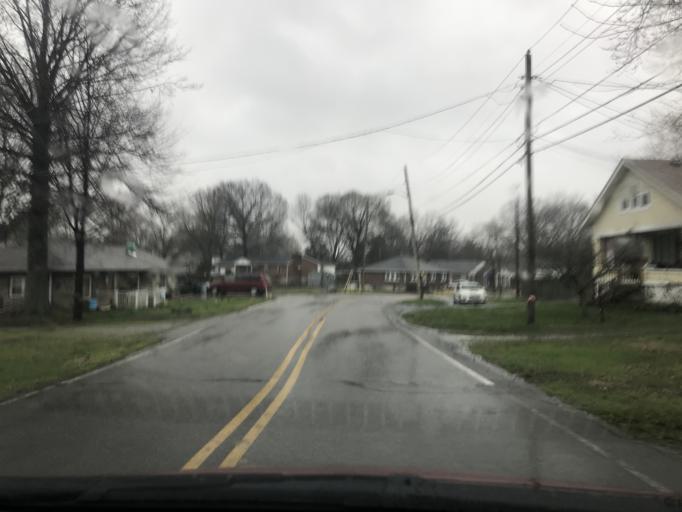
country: US
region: Indiana
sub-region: Clark County
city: Clarksville
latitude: 38.2766
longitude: -85.7621
